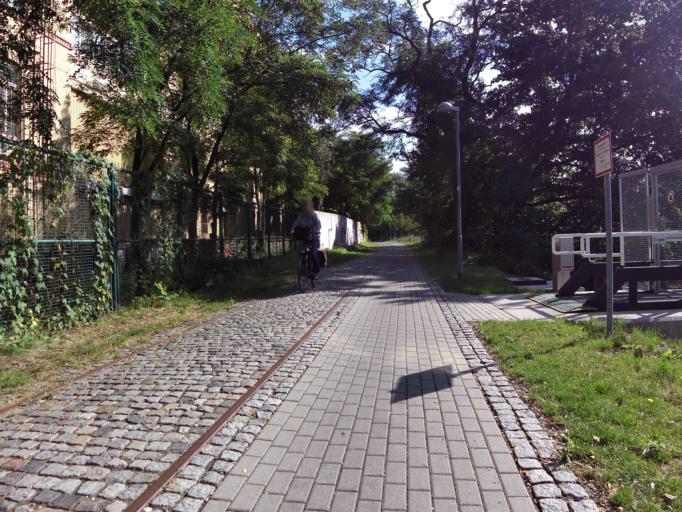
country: DE
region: Saxony-Anhalt
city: Wittenburg
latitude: 51.8642
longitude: 12.6249
